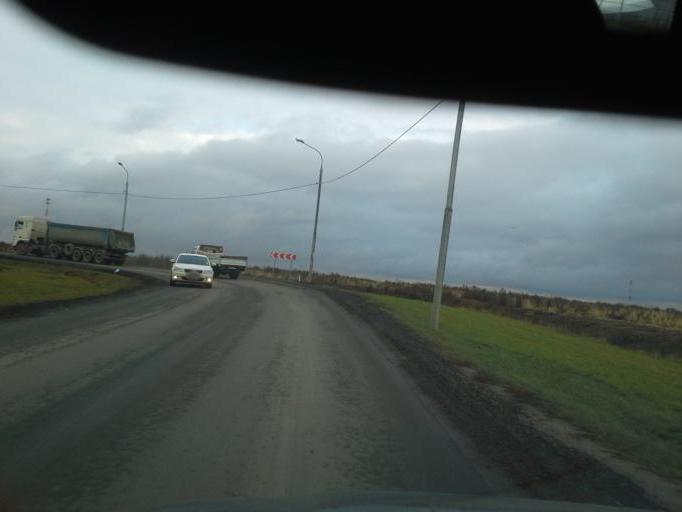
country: RU
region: Moskovskaya
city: Kommunarka
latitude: 55.5599
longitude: 37.4200
